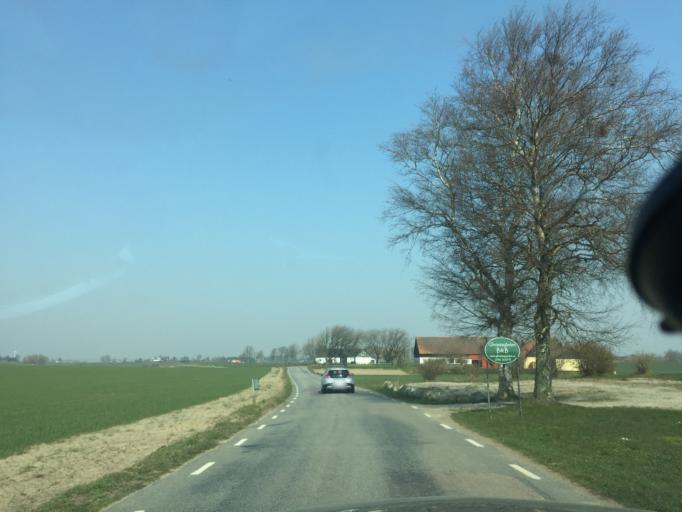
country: SE
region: Skane
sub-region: Simrishamns Kommun
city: Simrishamn
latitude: 55.4939
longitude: 14.2238
